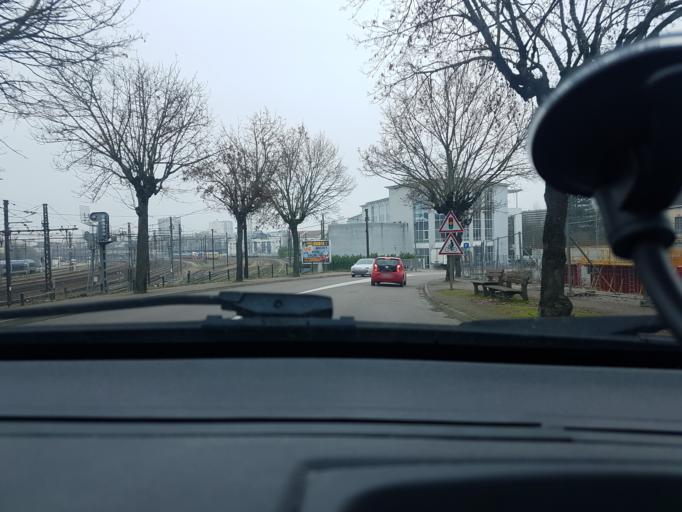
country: FR
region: Bourgogne
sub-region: Departement de Saone-et-Loire
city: Chalon-sur-Saone
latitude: 46.7770
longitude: 4.8448
